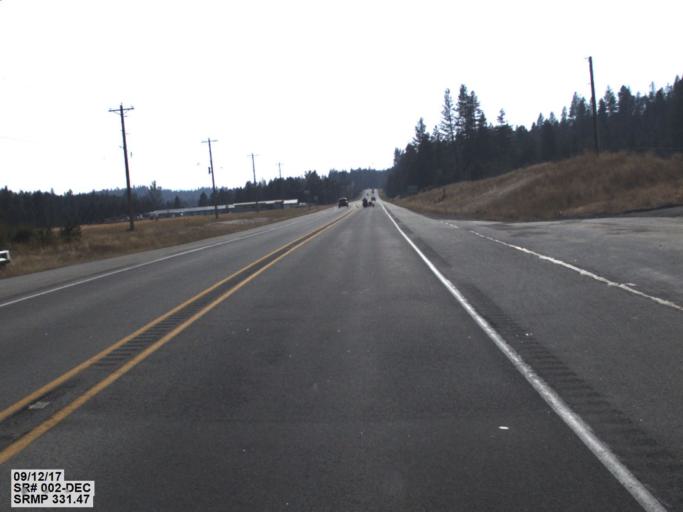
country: US
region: Washington
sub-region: Pend Oreille County
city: Newport
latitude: 48.1612
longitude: -117.0871
